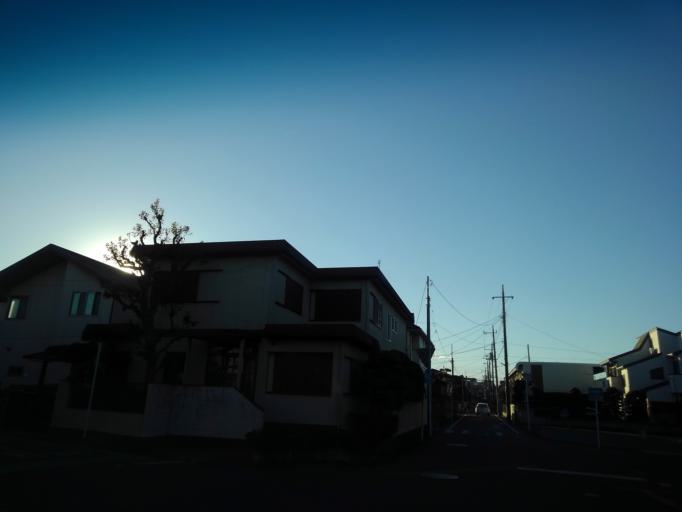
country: JP
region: Saitama
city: Tokorozawa
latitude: 35.8043
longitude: 139.4488
